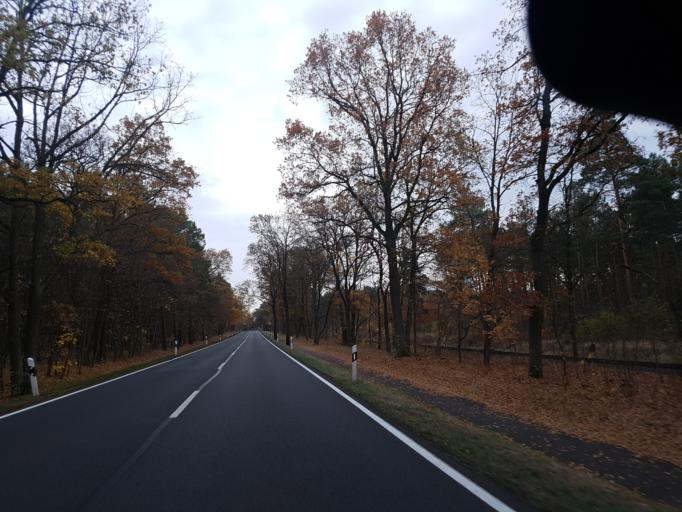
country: DE
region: Brandenburg
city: Treuenbrietzen
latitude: 52.0710
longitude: 12.8885
